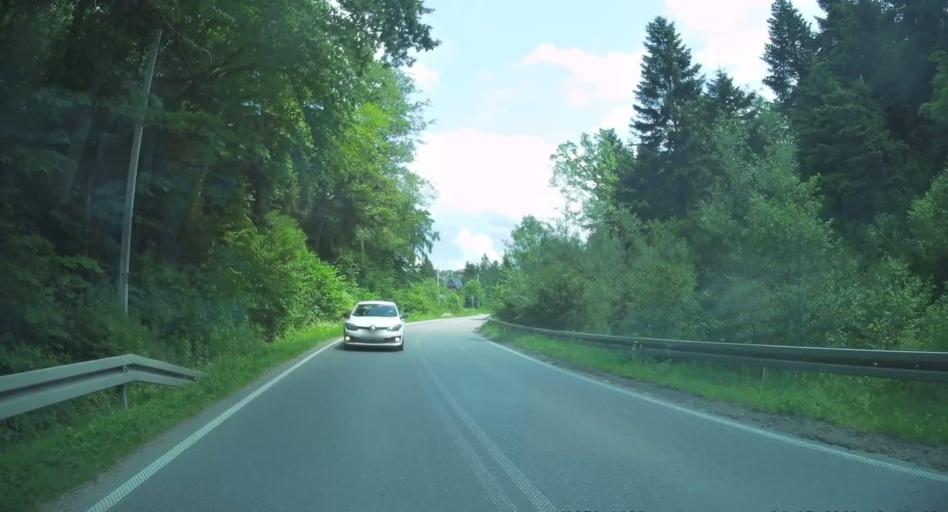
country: PL
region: Lesser Poland Voivodeship
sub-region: Powiat nowosadecki
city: Nowy Sacz
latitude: 49.6639
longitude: 20.7345
